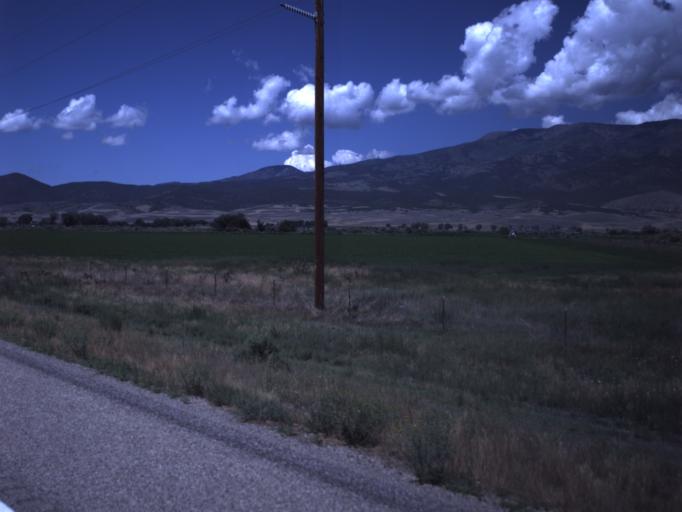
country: US
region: Utah
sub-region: Piute County
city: Junction
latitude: 38.1847
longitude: -112.2439
